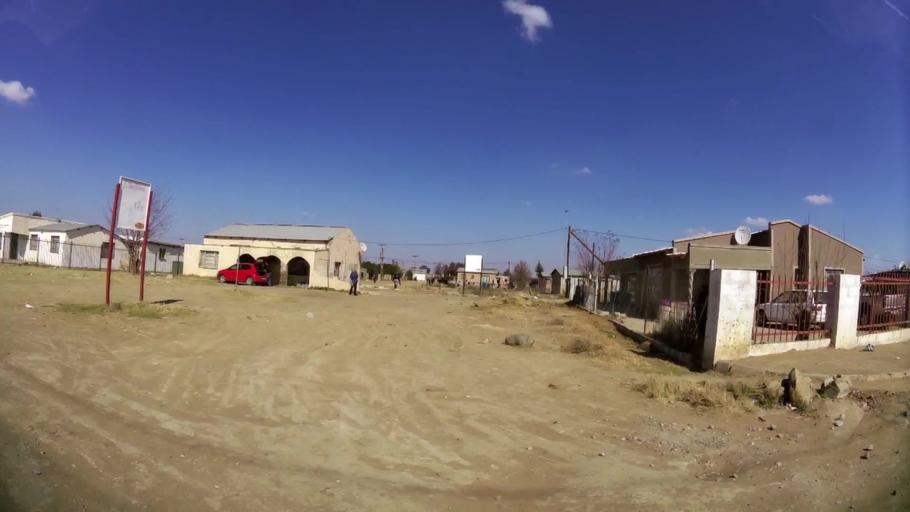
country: ZA
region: Orange Free State
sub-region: Mangaung Metropolitan Municipality
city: Bloemfontein
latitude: -29.1471
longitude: 26.2790
